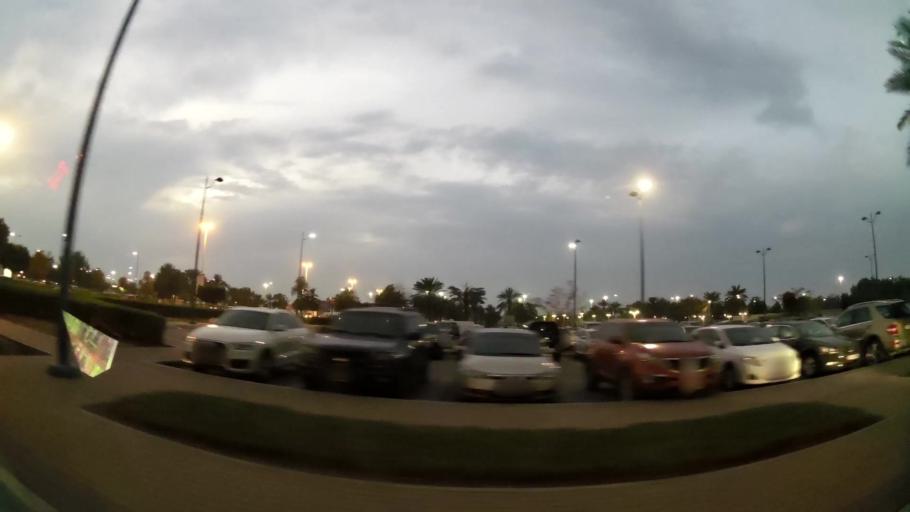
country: AE
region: Abu Dhabi
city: Abu Dhabi
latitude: 24.4940
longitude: 54.3605
